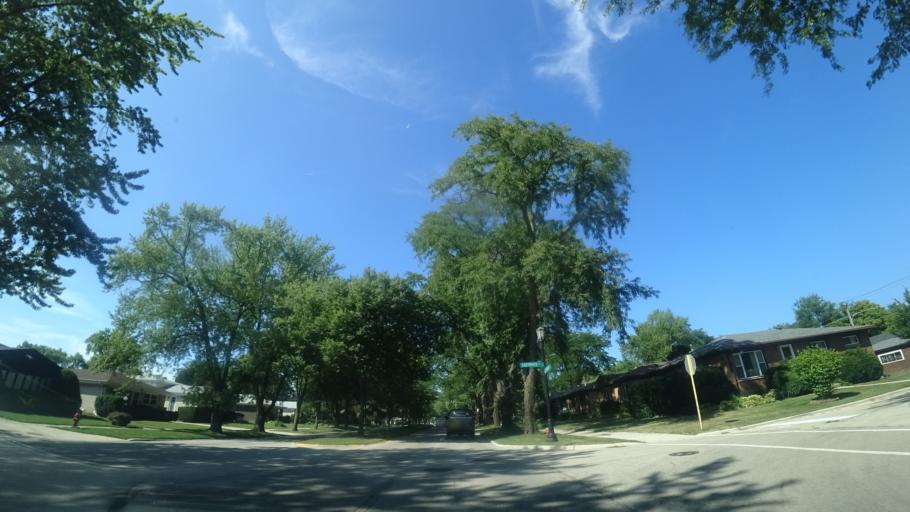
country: US
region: Illinois
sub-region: Cook County
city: Wilmette
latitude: 42.0595
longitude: -87.7273
